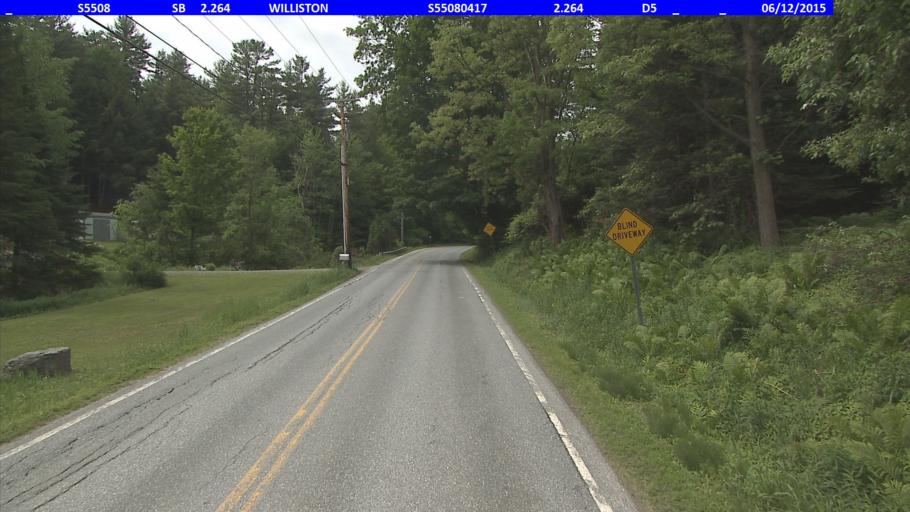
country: US
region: Vermont
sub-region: Chittenden County
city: Williston
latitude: 44.4635
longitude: -73.0489
